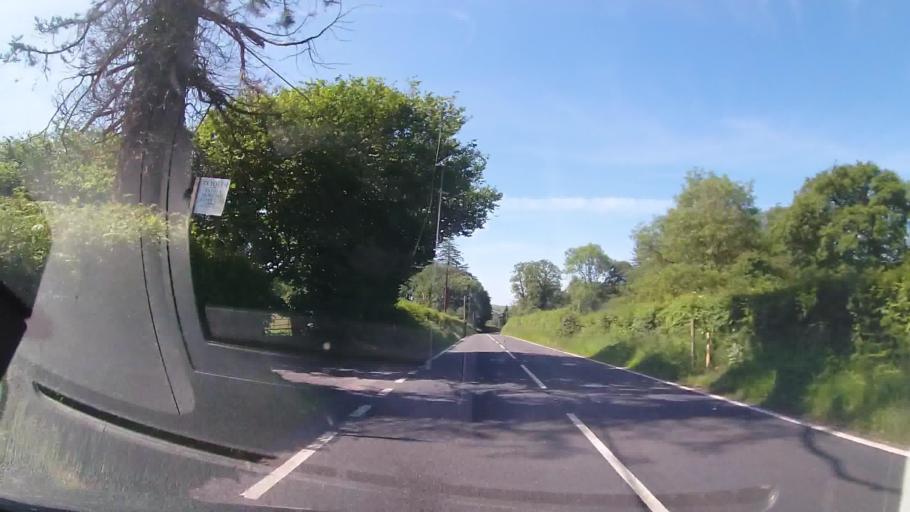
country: GB
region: Wales
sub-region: Gwynedd
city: Corris
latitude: 52.6497
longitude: -3.7076
